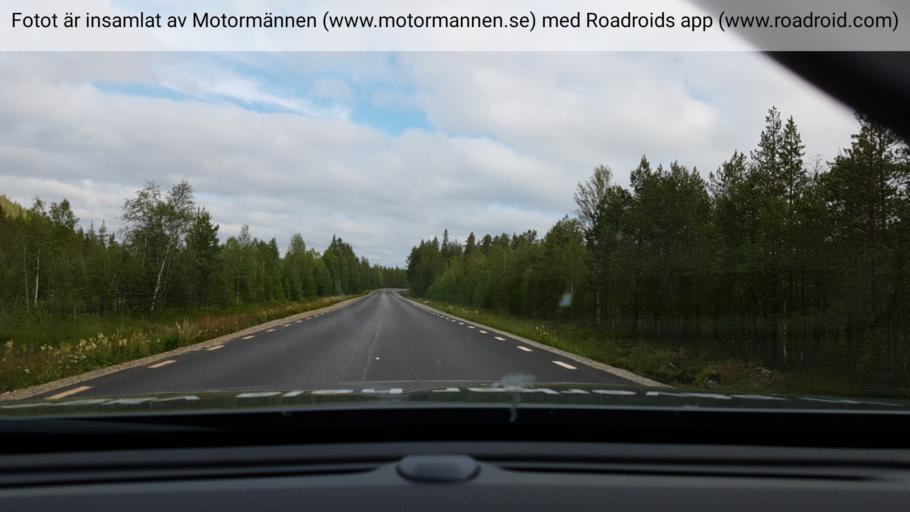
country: SE
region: Vaesterbotten
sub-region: Vindelns Kommun
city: Vindeln
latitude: 64.4251
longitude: 19.3528
